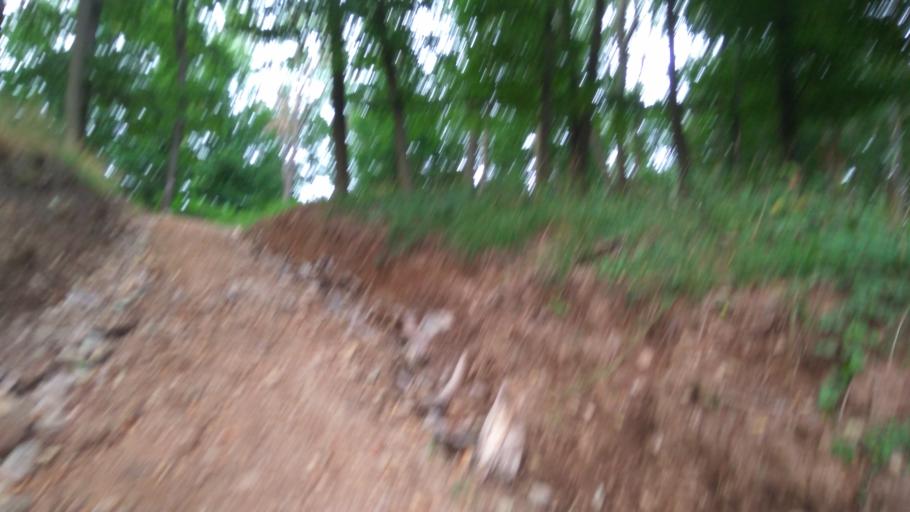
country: HU
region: Nograd
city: Diosjeno
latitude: 47.9924
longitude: 18.9798
